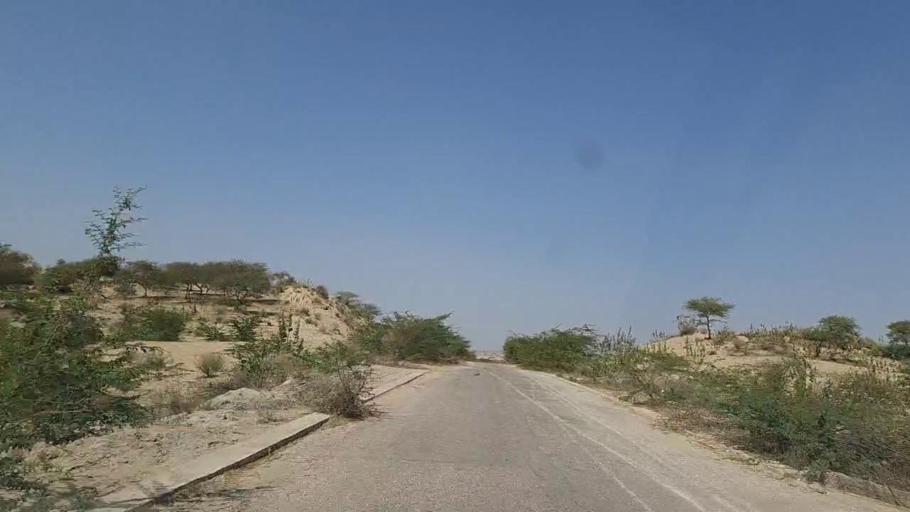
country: PK
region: Sindh
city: Naukot
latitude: 24.5834
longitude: 69.3190
